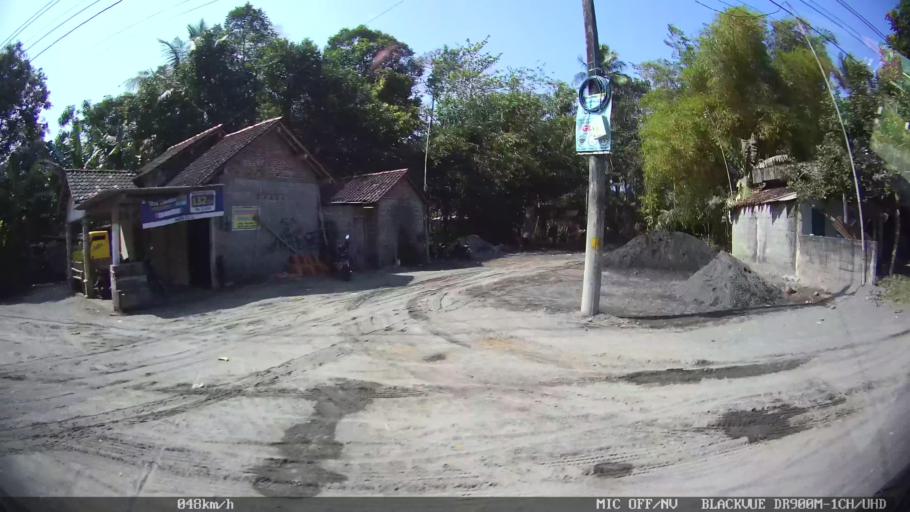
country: ID
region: Daerah Istimewa Yogyakarta
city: Srandakan
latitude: -7.9459
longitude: 110.2259
